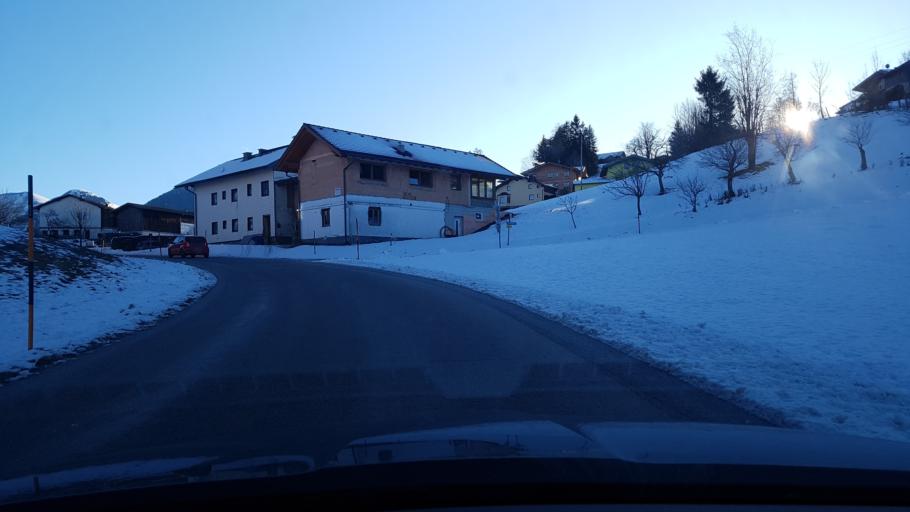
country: AT
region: Salzburg
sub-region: Politischer Bezirk Hallein
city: Kuchl
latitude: 47.6569
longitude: 13.1900
